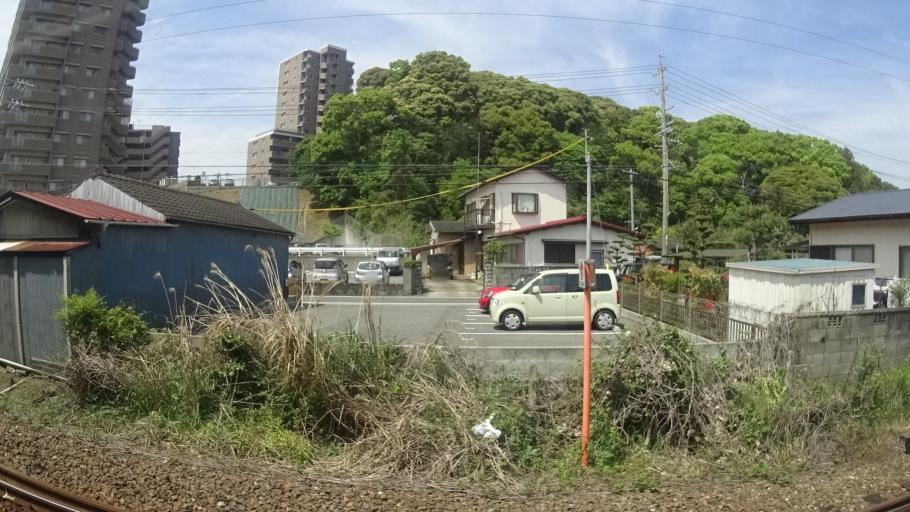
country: JP
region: Mie
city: Tsu-shi
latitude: 34.7380
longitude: 136.5106
